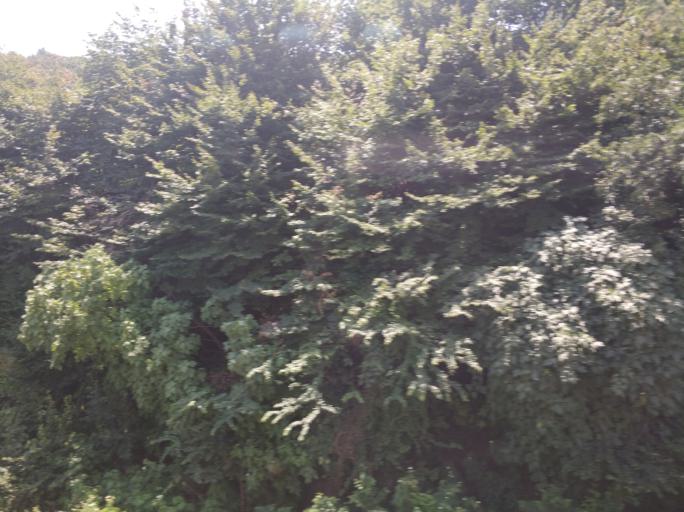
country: IR
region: Gilan
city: Pa'in-e Bazar-e Rudbar
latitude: 37.0049
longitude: 49.5913
